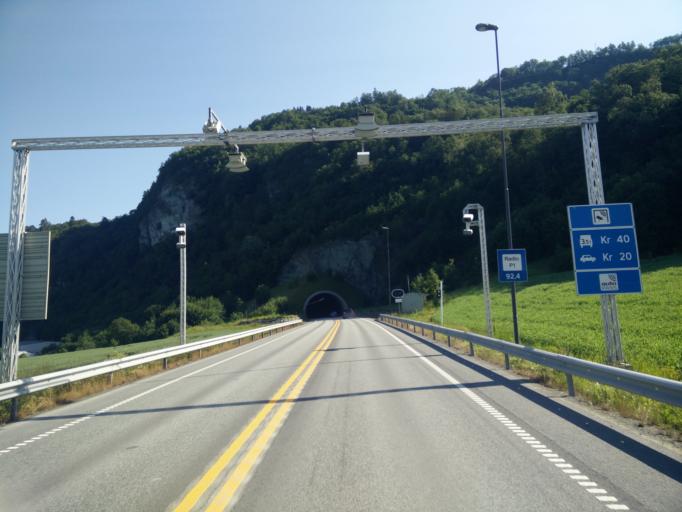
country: NO
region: Sor-Trondelag
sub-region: Melhus
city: Melhus
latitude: 63.3108
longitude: 10.1943
